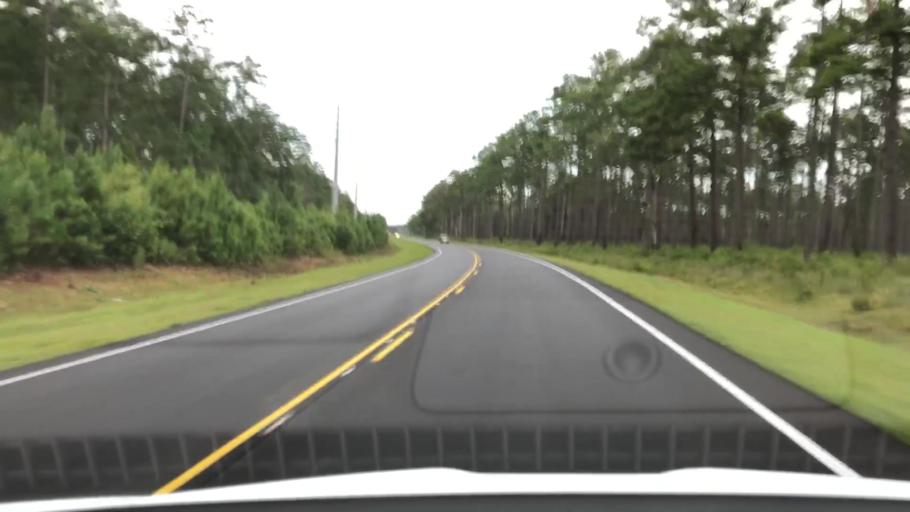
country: US
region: North Carolina
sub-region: Onslow County
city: Swansboro
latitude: 34.7753
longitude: -77.1001
